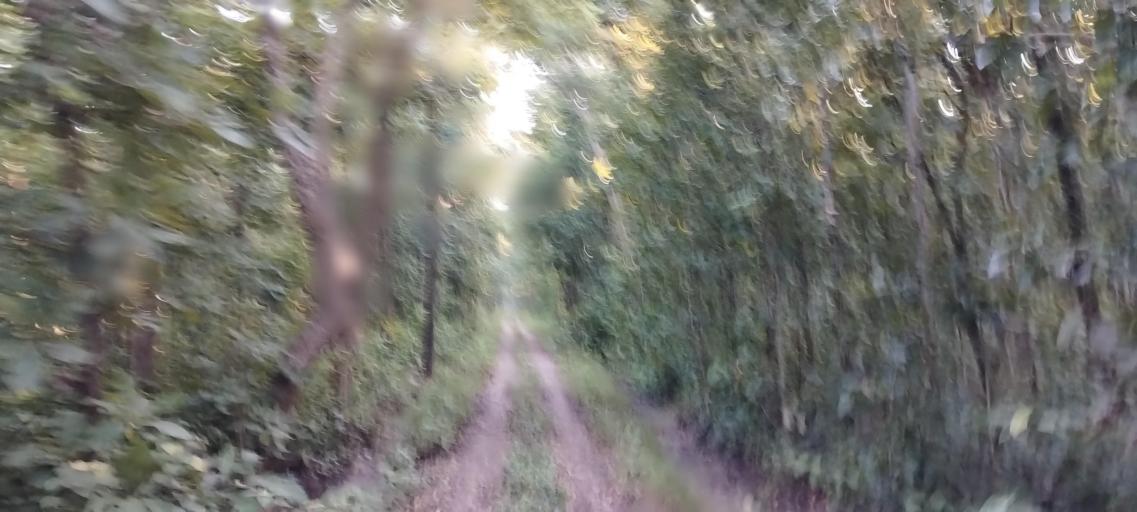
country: NP
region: Far Western
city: Tikapur
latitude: 28.4910
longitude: 81.2658
